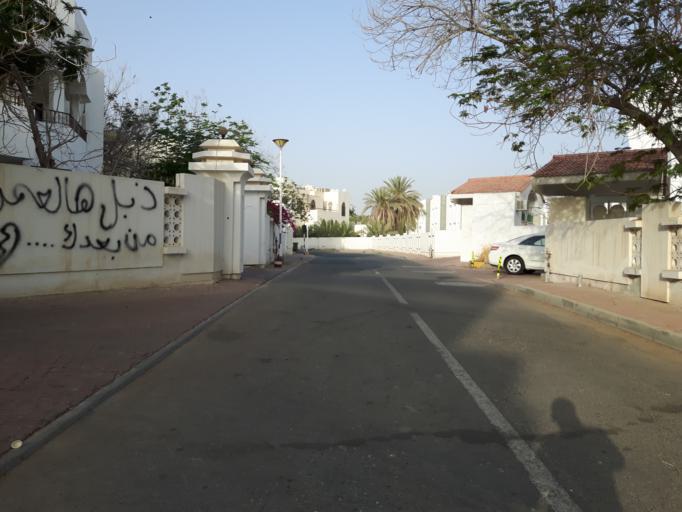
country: OM
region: Muhafazat Masqat
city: Bawshar
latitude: 23.6100
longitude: 58.4737
